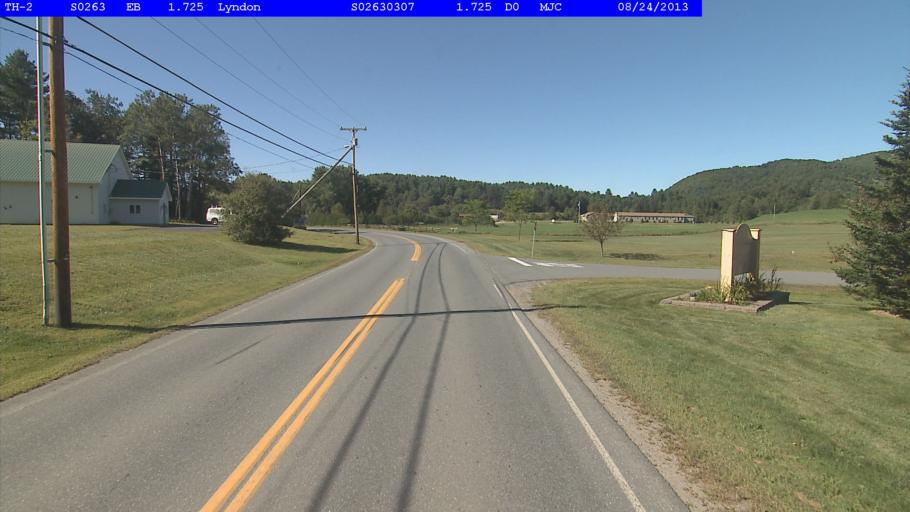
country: US
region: Vermont
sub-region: Caledonia County
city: Lyndon
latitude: 44.5095
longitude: -71.9922
